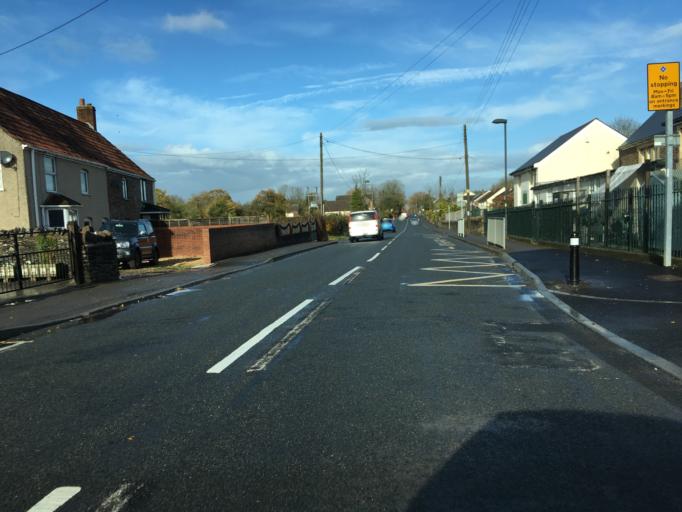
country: GB
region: England
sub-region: South Gloucestershire
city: Yate
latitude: 51.5518
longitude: -2.4357
